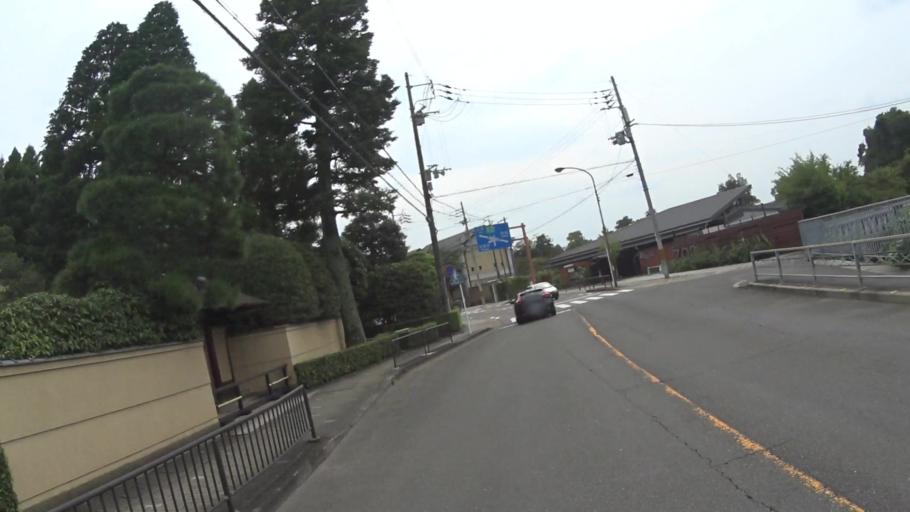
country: JP
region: Kyoto
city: Kyoto
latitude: 35.0126
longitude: 135.7888
